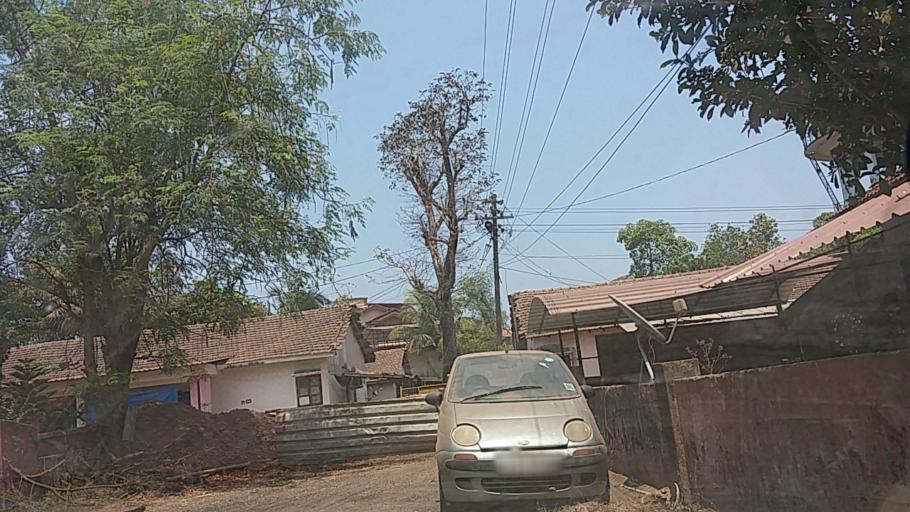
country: IN
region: Goa
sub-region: North Goa
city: Serula
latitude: 15.5234
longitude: 73.8352
